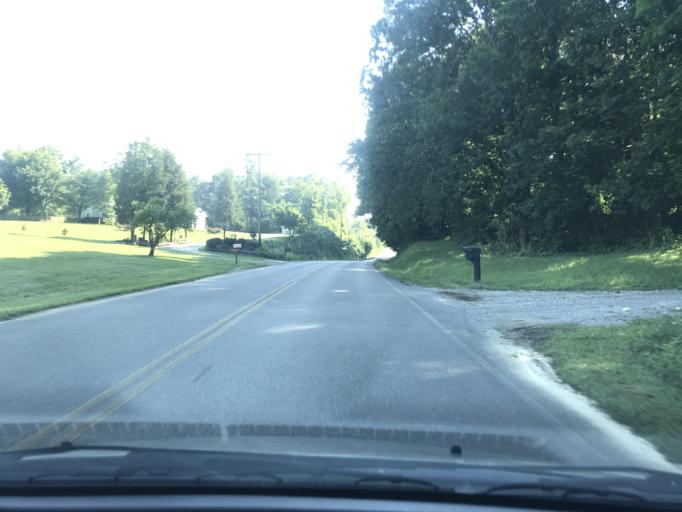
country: US
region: Tennessee
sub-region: Loudon County
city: Loudon
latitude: 35.8083
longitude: -84.3482
